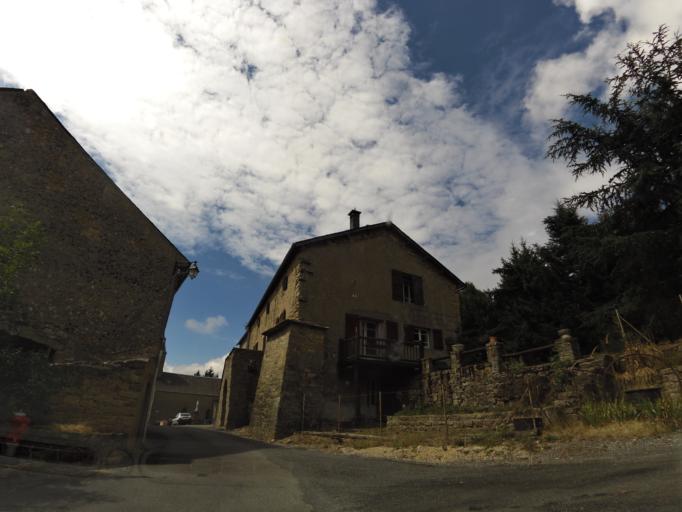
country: FR
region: Languedoc-Roussillon
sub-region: Departement de la Lozere
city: Meyrueis
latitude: 44.1152
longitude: 3.4785
